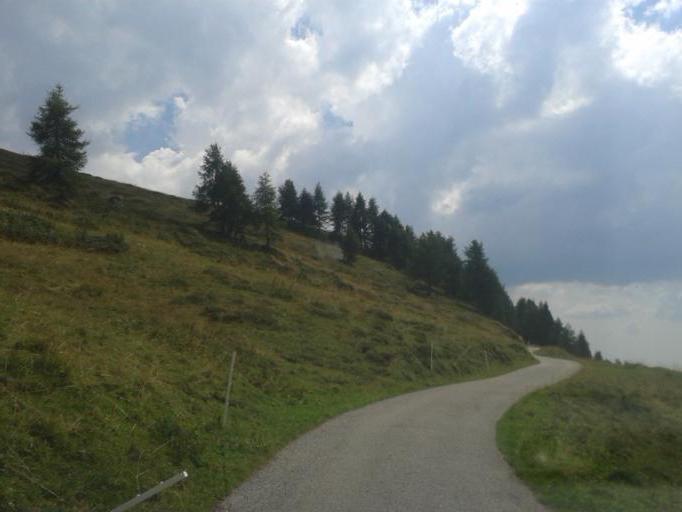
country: IT
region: Trentino-Alto Adige
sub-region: Provincia di Trento
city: Lodrone-Darzo
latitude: 45.8722
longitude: 10.5234
